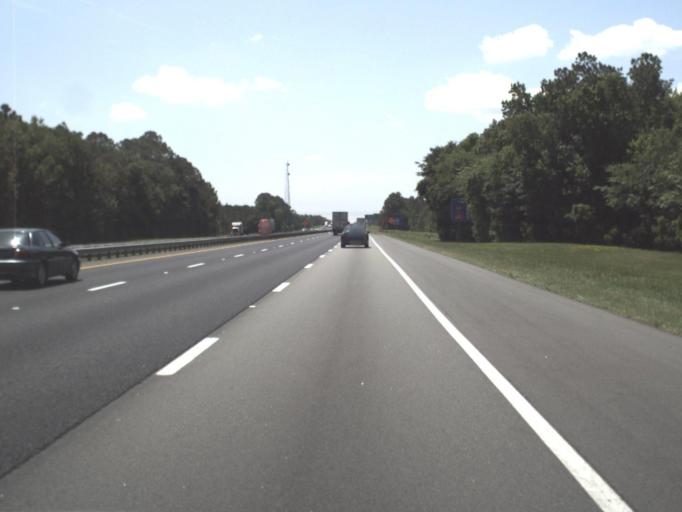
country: US
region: Florida
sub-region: Nassau County
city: Yulee
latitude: 30.6287
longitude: -81.6534
